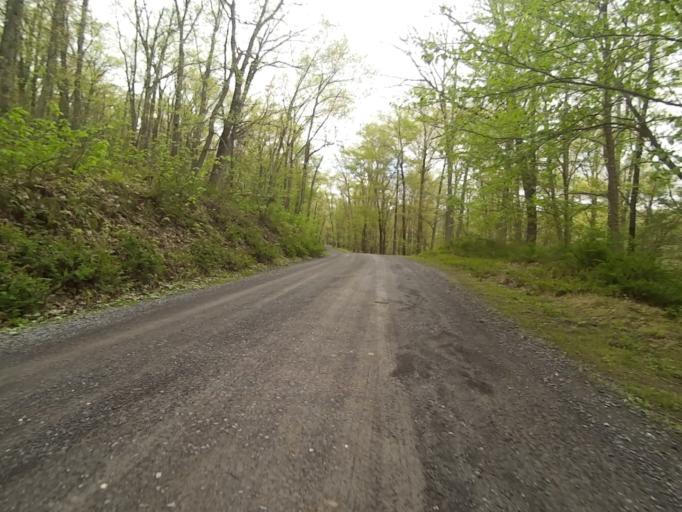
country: US
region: Pennsylvania
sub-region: Centre County
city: Boalsburg
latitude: 40.7589
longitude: -77.7577
